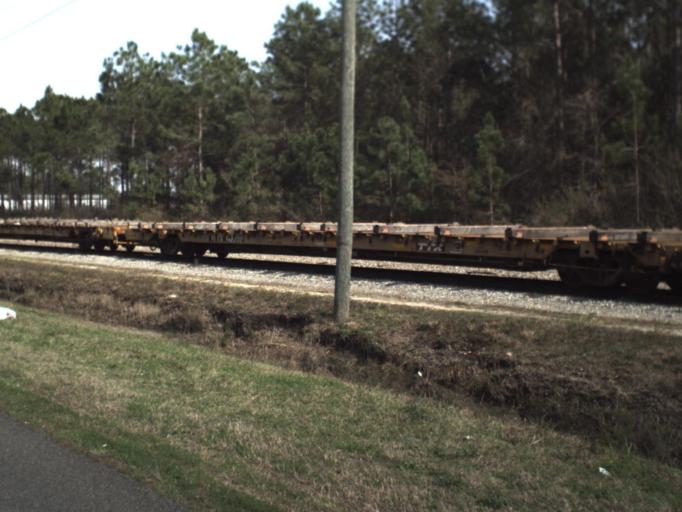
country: US
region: Florida
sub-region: Bay County
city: Hiland Park
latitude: 30.2112
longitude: -85.6101
